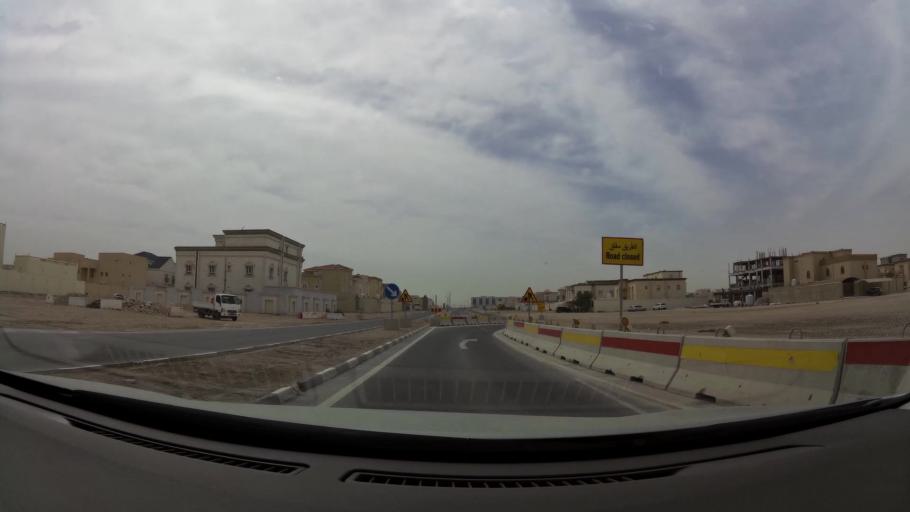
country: QA
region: Al Wakrah
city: Al Wukayr
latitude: 25.2081
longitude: 51.4721
